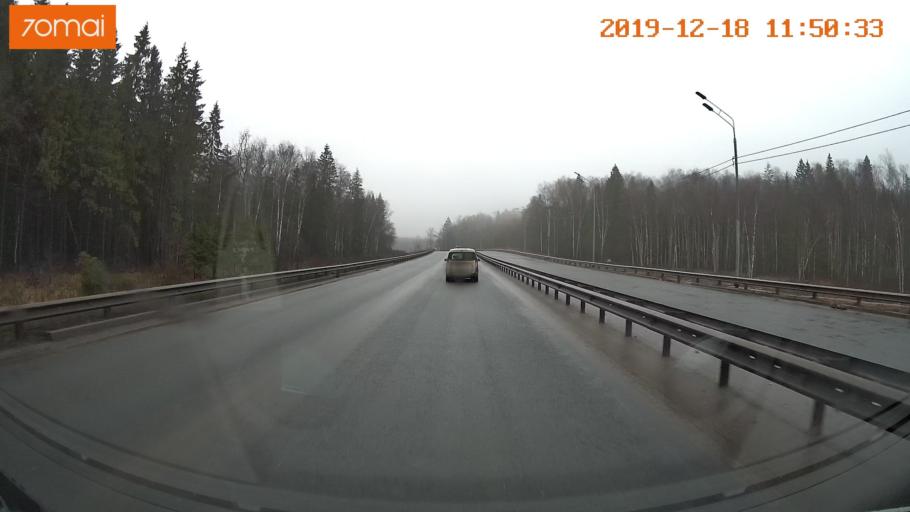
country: RU
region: Moskovskaya
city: Yershovo
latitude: 55.7868
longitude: 36.9195
